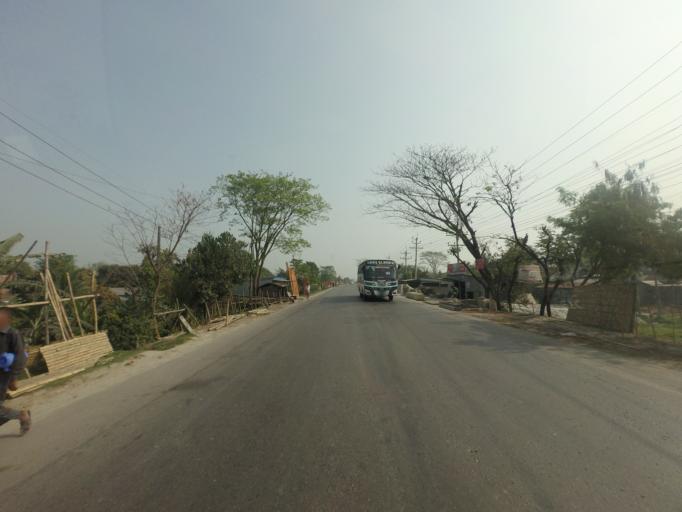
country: BD
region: Dhaka
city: Narsingdi
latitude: 23.8161
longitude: 90.5967
